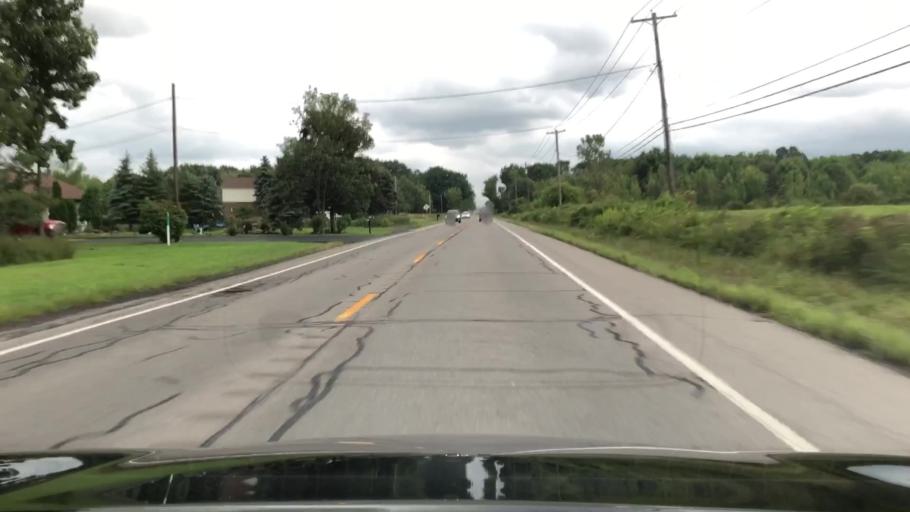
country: US
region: New York
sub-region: Erie County
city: Orchard Park
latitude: 42.8004
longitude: -78.6969
